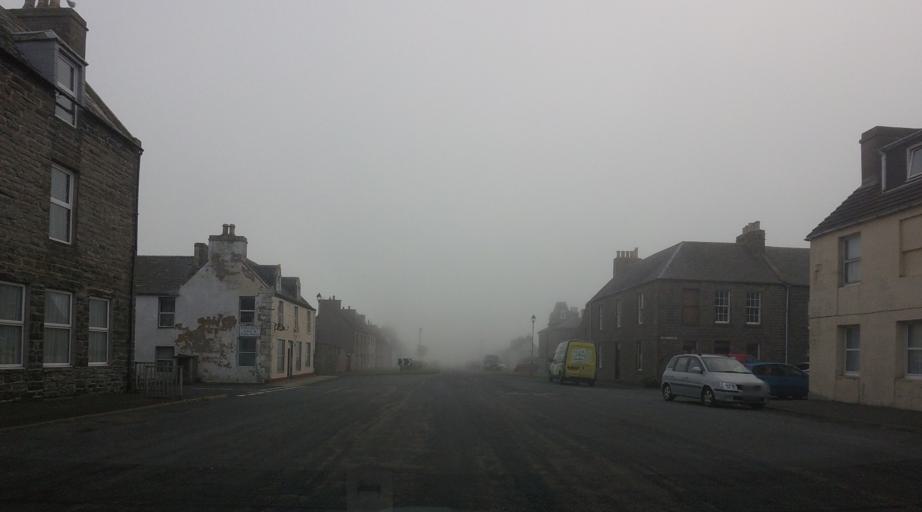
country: GB
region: Scotland
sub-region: Highland
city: Wick
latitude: 58.3016
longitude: -3.2847
